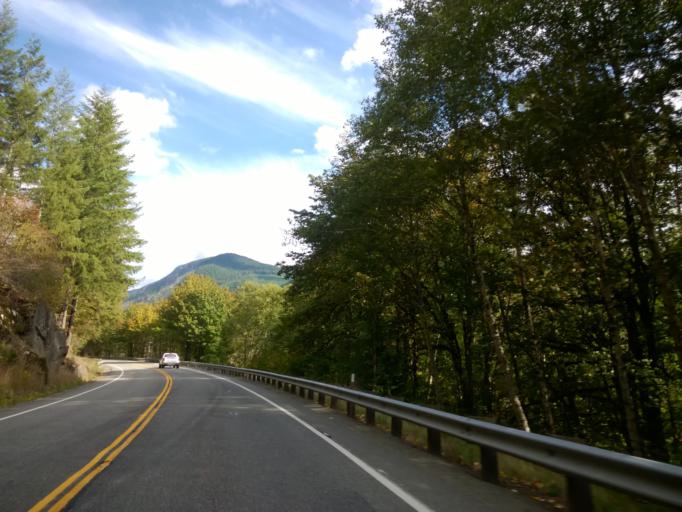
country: US
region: Washington
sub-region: Snohomish County
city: Gold Bar
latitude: 47.7147
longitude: -121.2695
